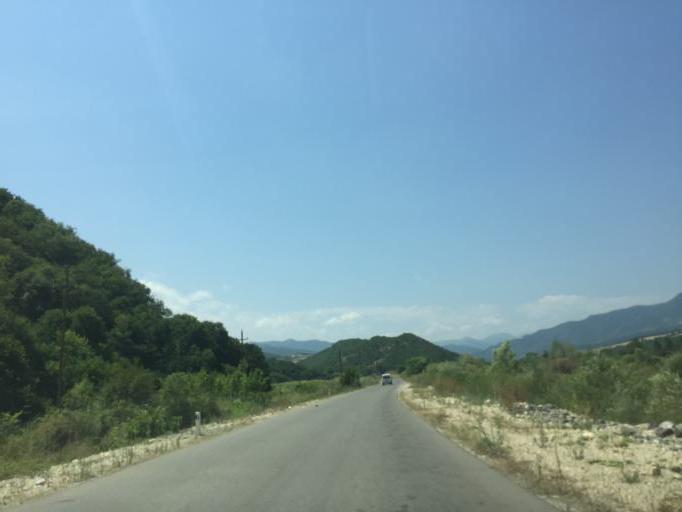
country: AZ
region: Tartar Rayon
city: Martakert
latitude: 40.1389
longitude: 46.5117
